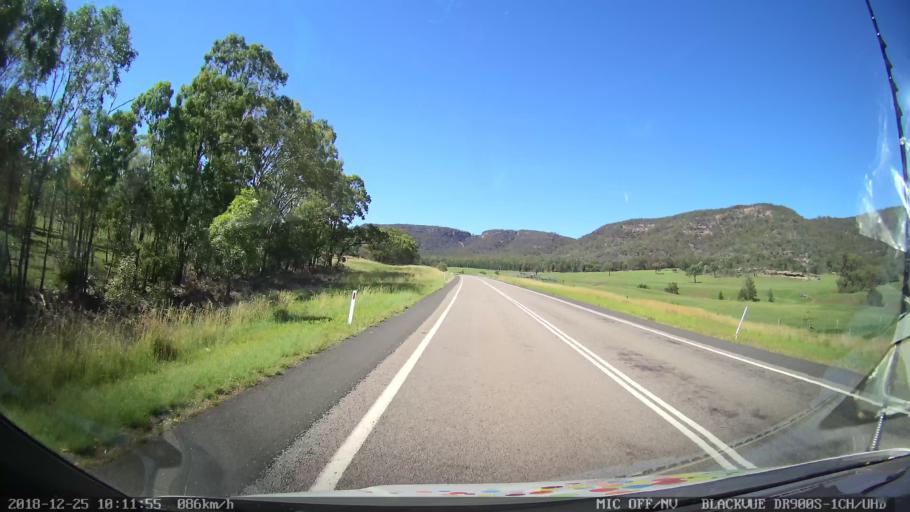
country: AU
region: New South Wales
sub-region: Muswellbrook
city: Denman
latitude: -32.3226
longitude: 150.5292
